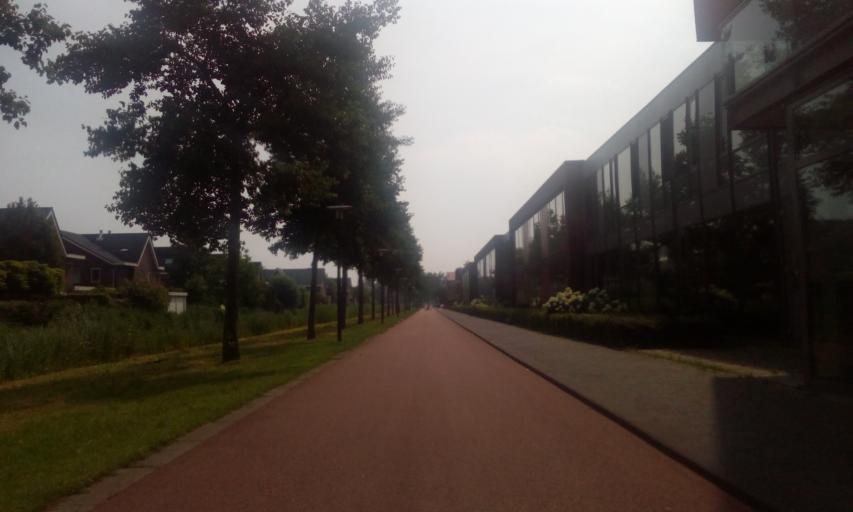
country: NL
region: South Holland
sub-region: Gemeente Capelle aan den IJssel
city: Capelle aan den IJssel
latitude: 51.9822
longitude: 4.5876
